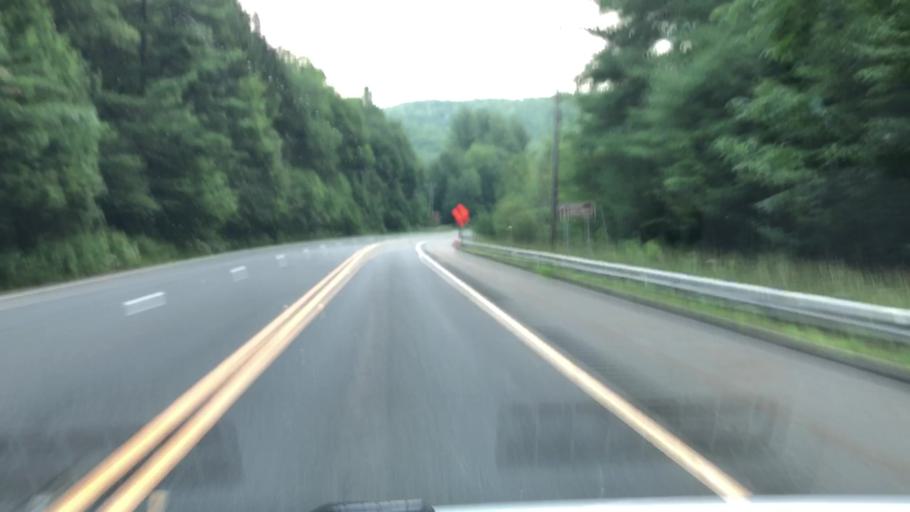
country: US
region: Massachusetts
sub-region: Berkshire County
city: Hinsdale
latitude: 42.4884
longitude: -72.9786
